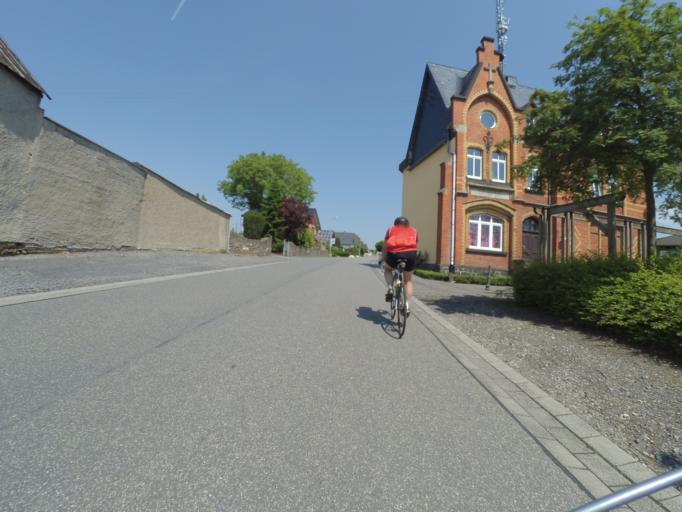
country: DE
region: Rheinland-Pfalz
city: Reudelsterz
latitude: 50.3171
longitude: 7.1557
